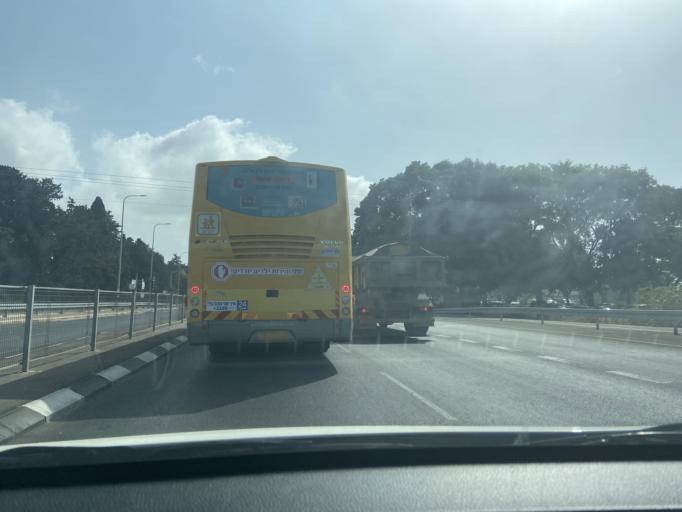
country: IL
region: Northern District
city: Nahariya
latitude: 33.0341
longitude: 35.1043
